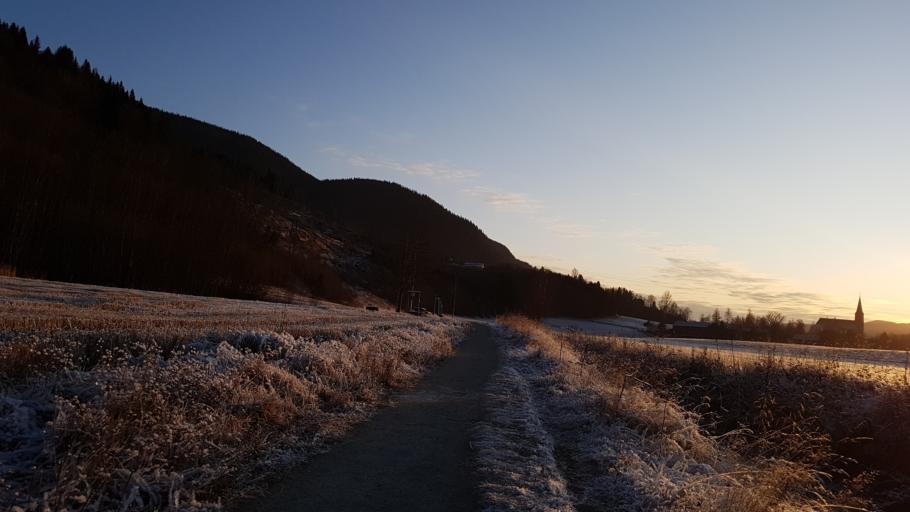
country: NO
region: Sor-Trondelag
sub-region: Melhus
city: Melhus
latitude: 63.2800
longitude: 10.3005
